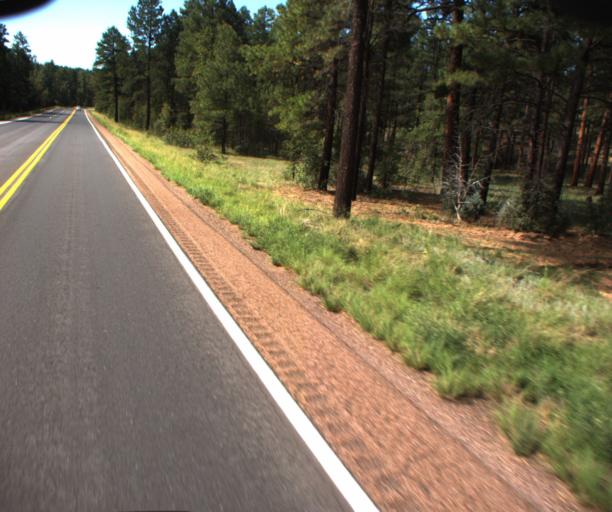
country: US
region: Arizona
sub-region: Navajo County
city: Show Low
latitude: 34.1890
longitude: -110.0917
